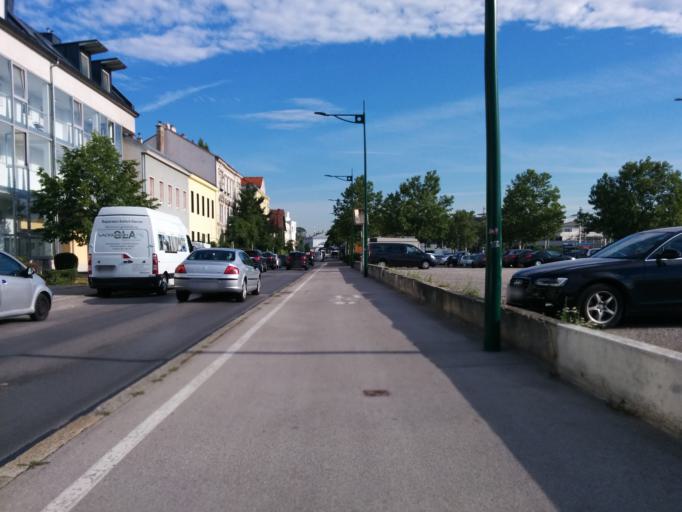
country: AT
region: Lower Austria
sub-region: Politischer Bezirk Modling
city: Modling
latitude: 48.0829
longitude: 16.2963
